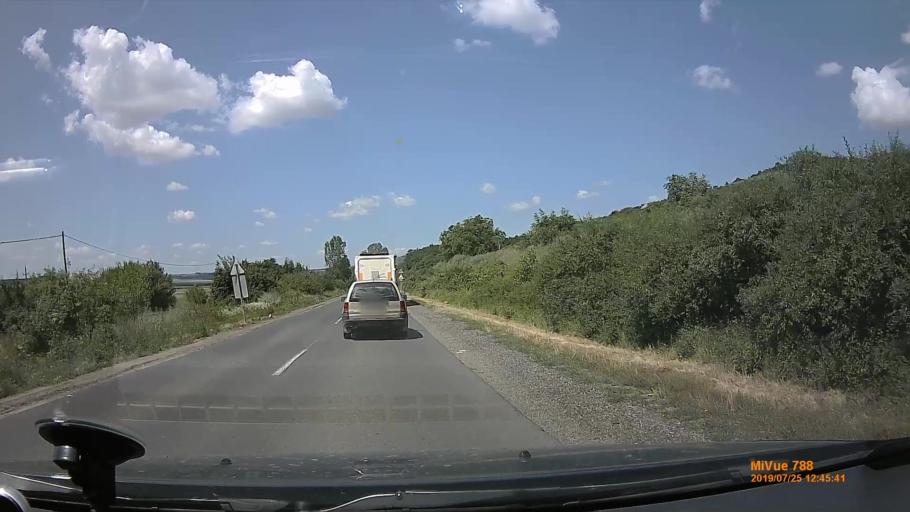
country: HU
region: Borsod-Abauj-Zemplen
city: Tallya
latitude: 48.2438
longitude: 21.2033
